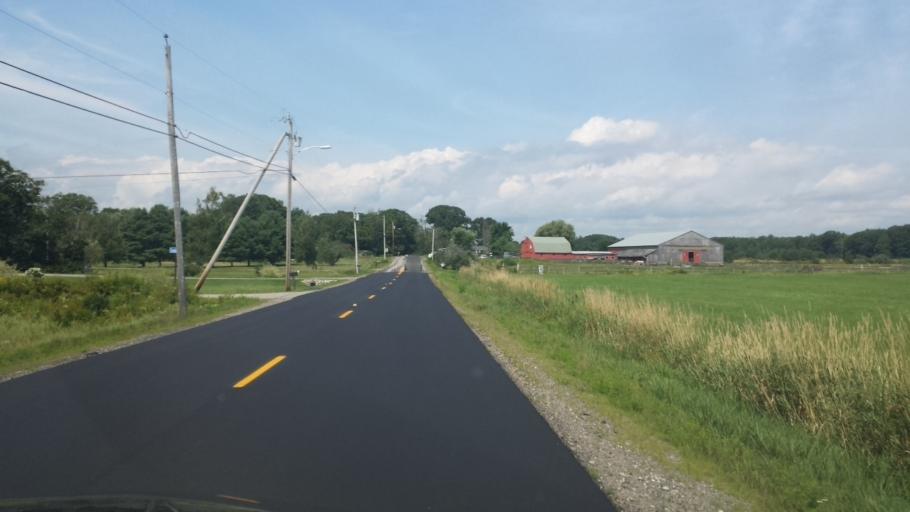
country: US
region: Maine
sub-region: York County
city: Biddeford
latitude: 43.4309
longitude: -70.4028
